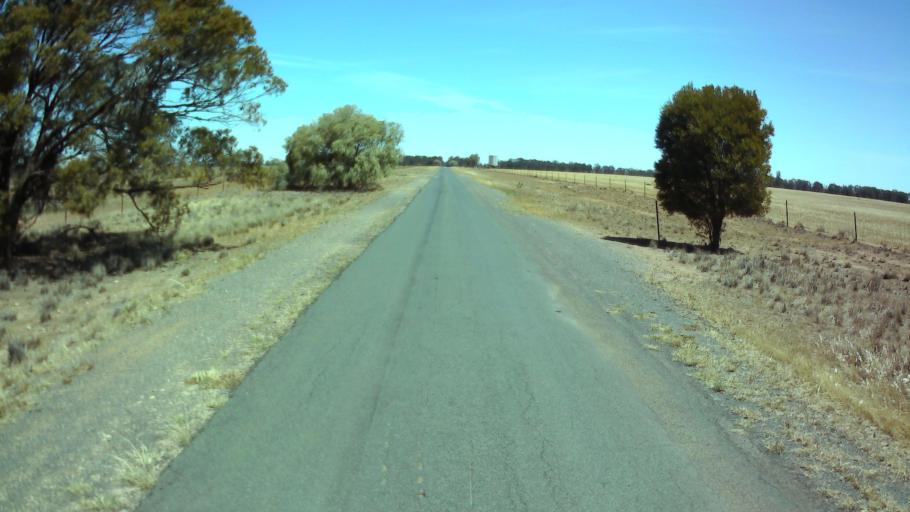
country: AU
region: New South Wales
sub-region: Weddin
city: Grenfell
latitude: -33.8555
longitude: 147.6948
